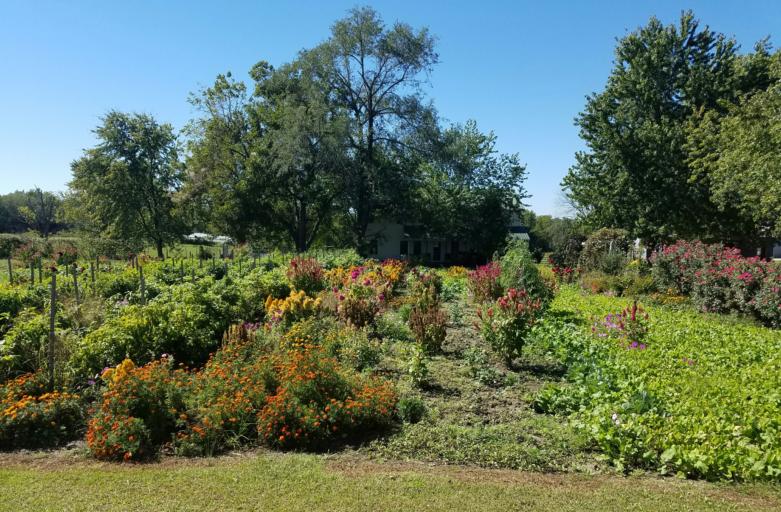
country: US
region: Missouri
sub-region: Carroll County
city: Carrollton
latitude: 39.4429
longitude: -93.4766
